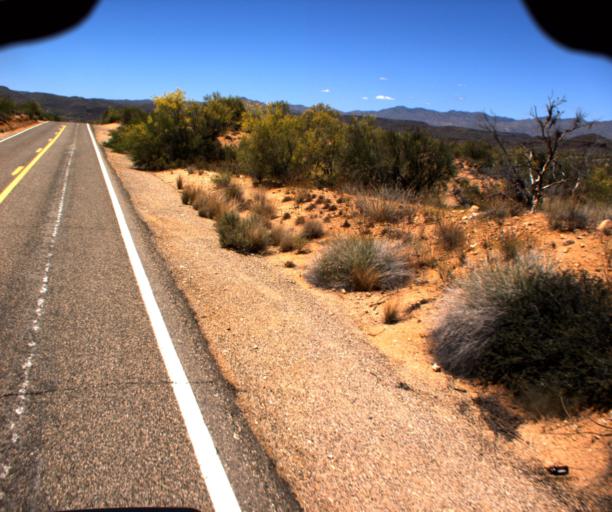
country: US
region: Arizona
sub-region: Yavapai County
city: Bagdad
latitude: 34.4628
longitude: -113.0421
